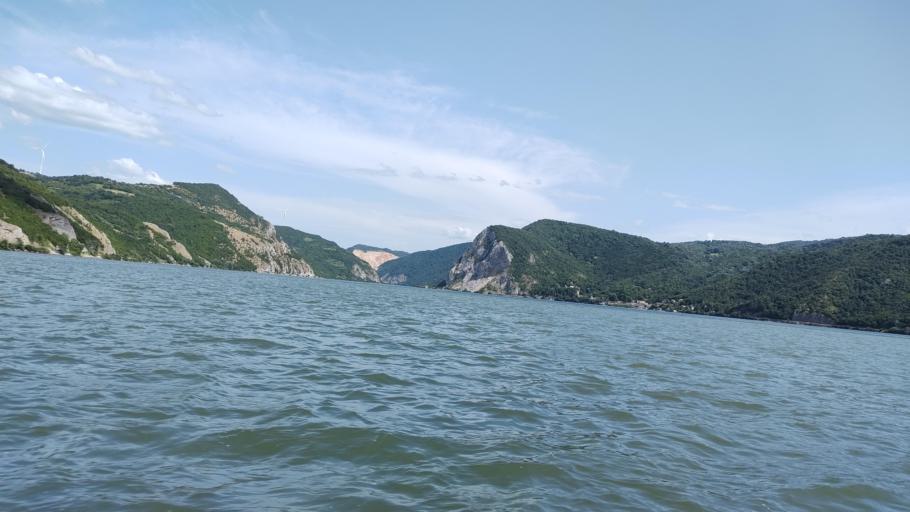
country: RO
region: Caras-Severin
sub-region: Comuna Pescari
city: Coronini
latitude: 44.6708
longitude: 21.6747
